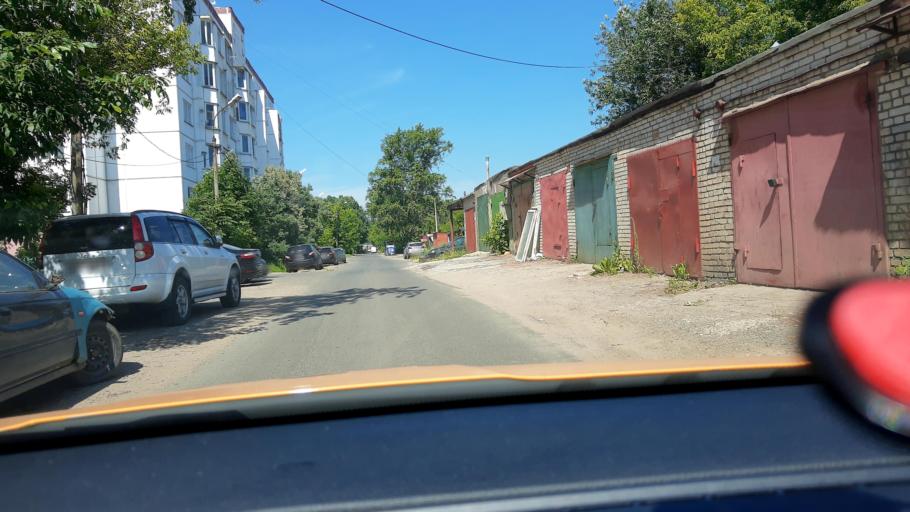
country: RU
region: Moscow
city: Severnyy
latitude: 55.9492
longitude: 37.5298
